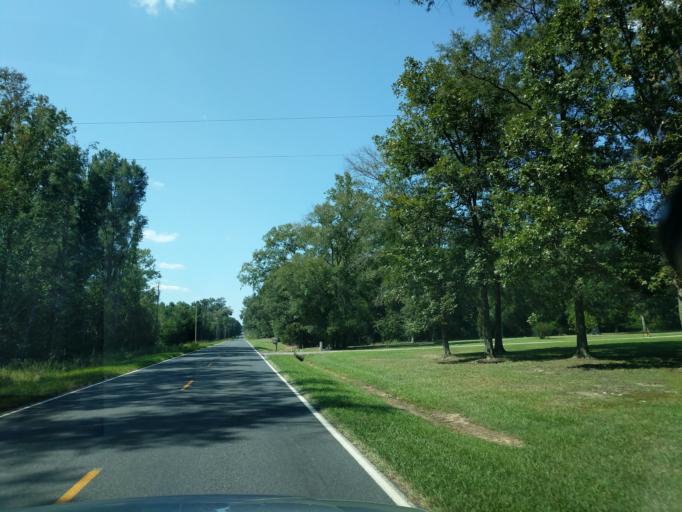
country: US
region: South Carolina
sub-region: Lexington County
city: Leesville
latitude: 34.0322
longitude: -81.5365
